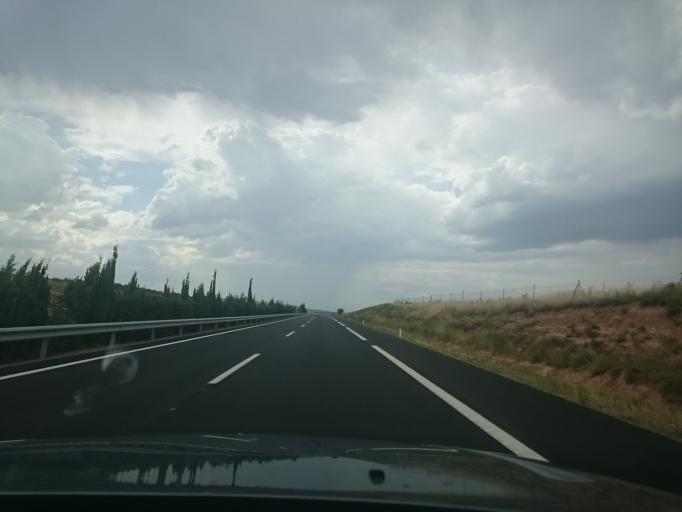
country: ES
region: La Rioja
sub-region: Provincia de La Rioja
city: Aldeanueva de Ebro
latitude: 42.2074
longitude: -1.8680
